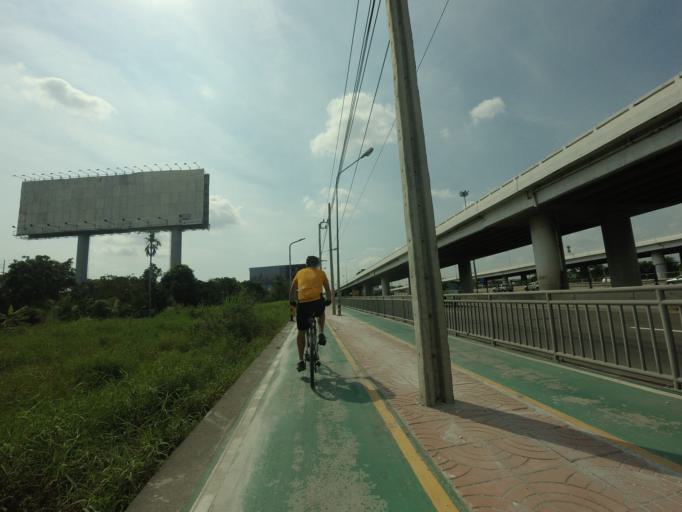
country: TH
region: Bangkok
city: Lat Krabang
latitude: 13.7293
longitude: 100.7569
